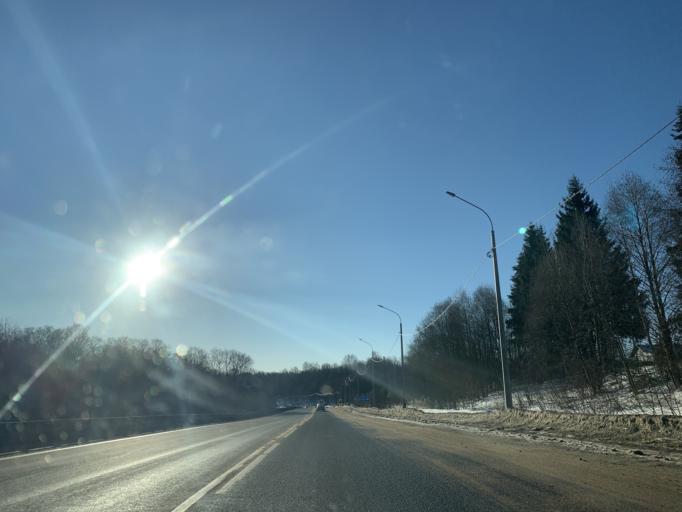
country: RU
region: Jaroslavl
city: Konstantinovskiy
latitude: 57.8106
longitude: 39.5724
